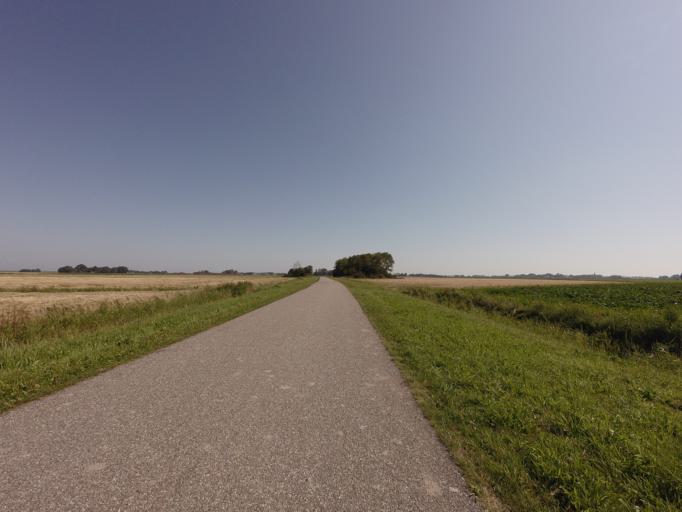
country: NL
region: Friesland
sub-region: Gemeente Dongeradeel
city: Holwerd
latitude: 53.3675
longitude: 5.9336
